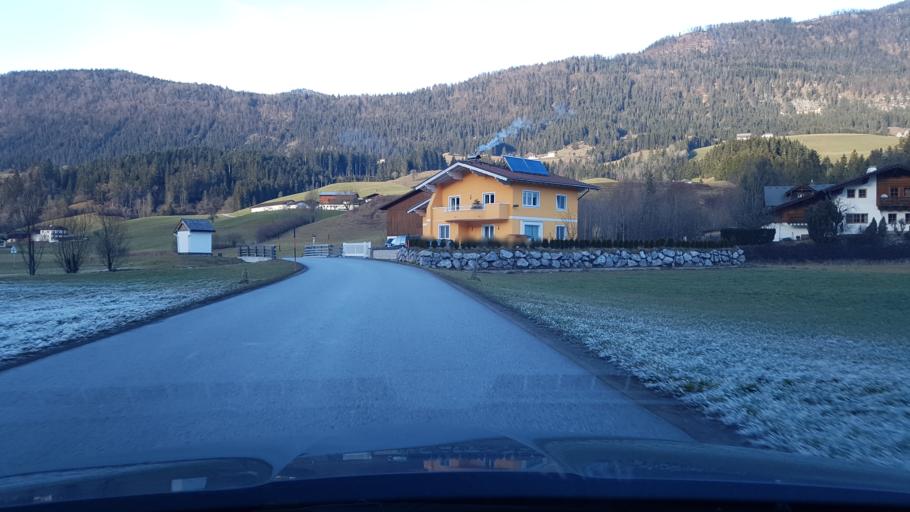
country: AT
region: Salzburg
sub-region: Politischer Bezirk Hallein
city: Abtenau
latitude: 47.5912
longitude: 13.3326
